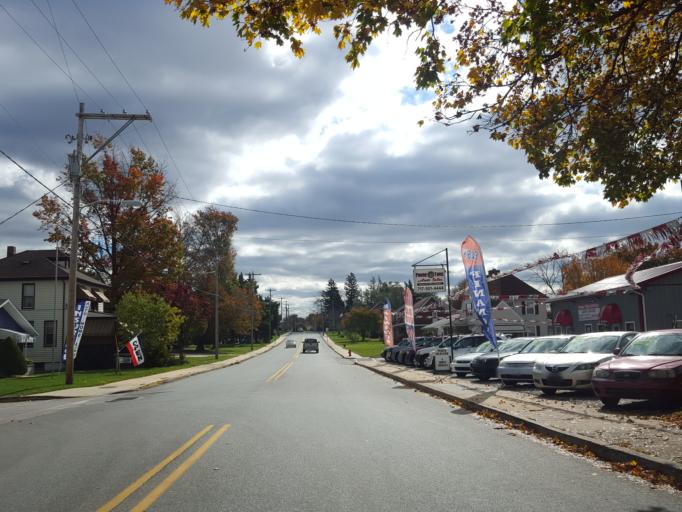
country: US
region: Pennsylvania
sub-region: York County
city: Red Lion
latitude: 39.8923
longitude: -76.5981
